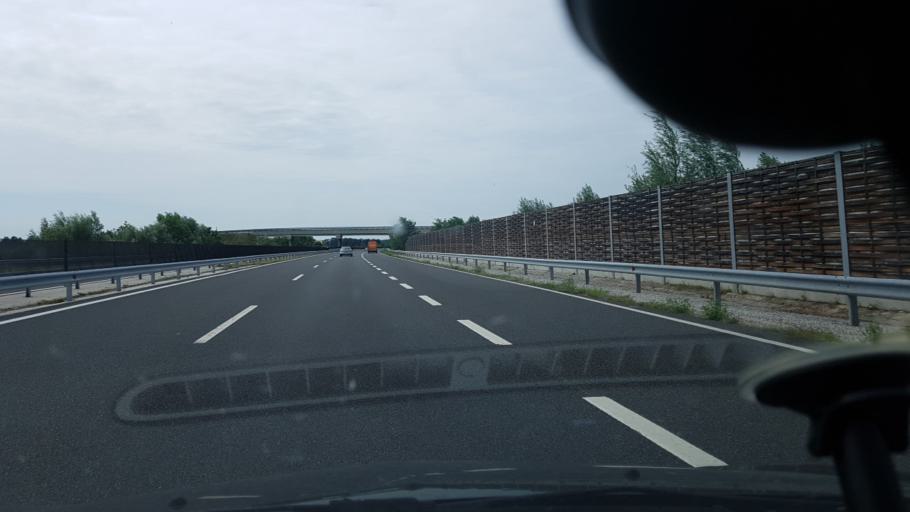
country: HU
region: Somogy
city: Balatonbereny
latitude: 46.6307
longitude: 17.2789
